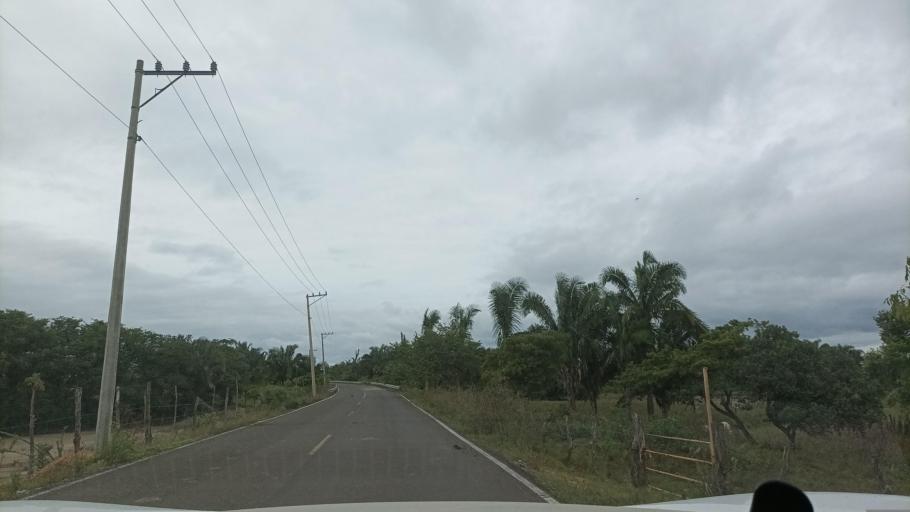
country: MX
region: Veracruz
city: Hidalgotitlan
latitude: 17.8102
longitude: -94.5616
